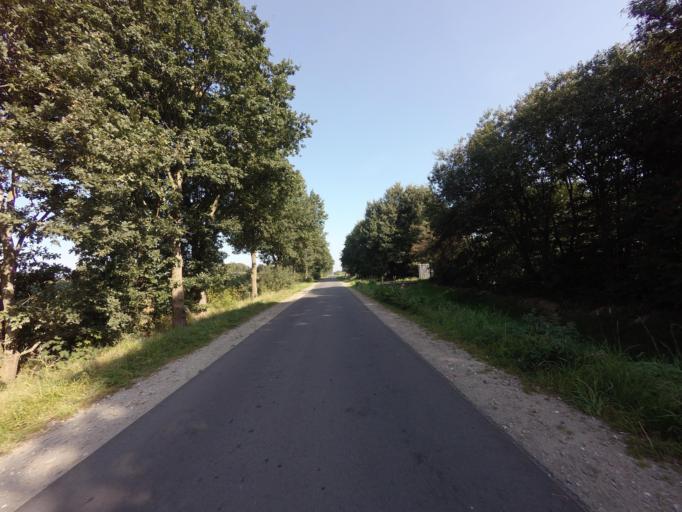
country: DE
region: Lower Saxony
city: Laar
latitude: 52.5769
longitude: 6.7801
